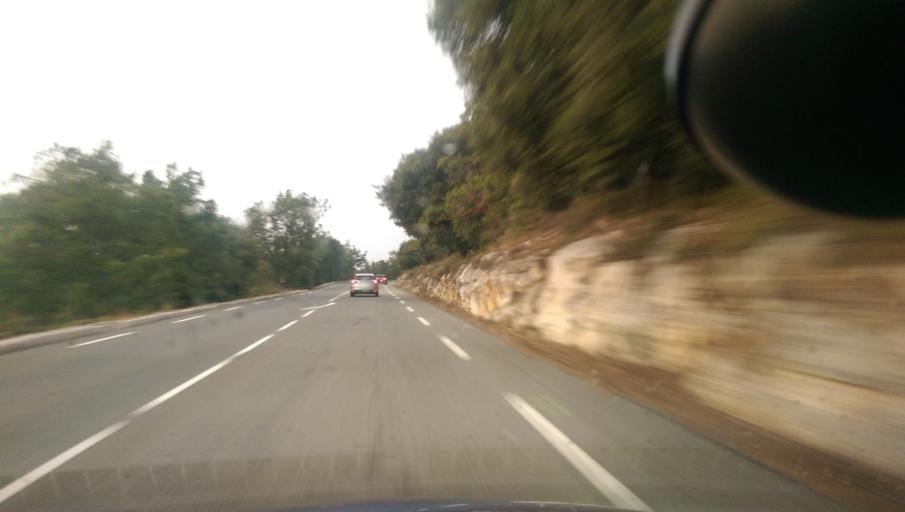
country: FR
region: Provence-Alpes-Cote d'Azur
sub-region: Departement des Alpes-Maritimes
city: Grasse
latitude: 43.6803
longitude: 6.8931
